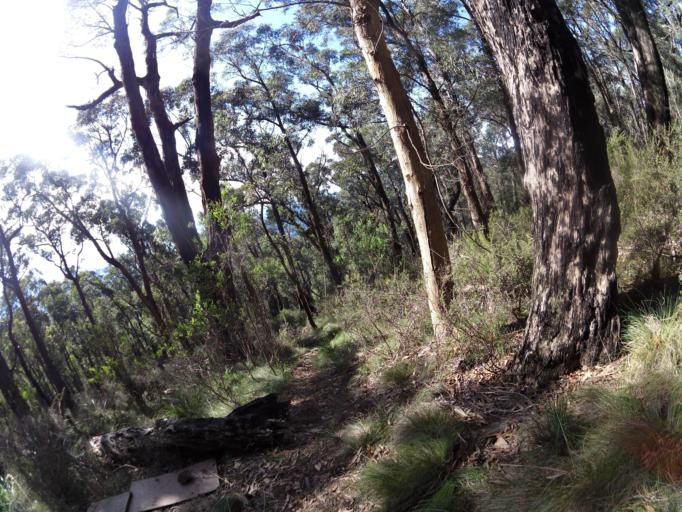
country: AU
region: Victoria
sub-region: Yarra Ranges
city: Ferny Creek
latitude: -37.8707
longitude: 145.3187
